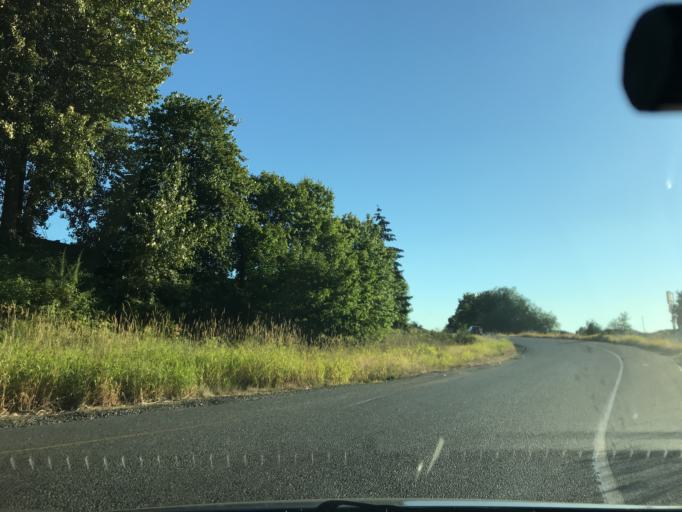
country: US
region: Washington
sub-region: Pierce County
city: Bonney Lake
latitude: 47.1986
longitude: -122.2082
